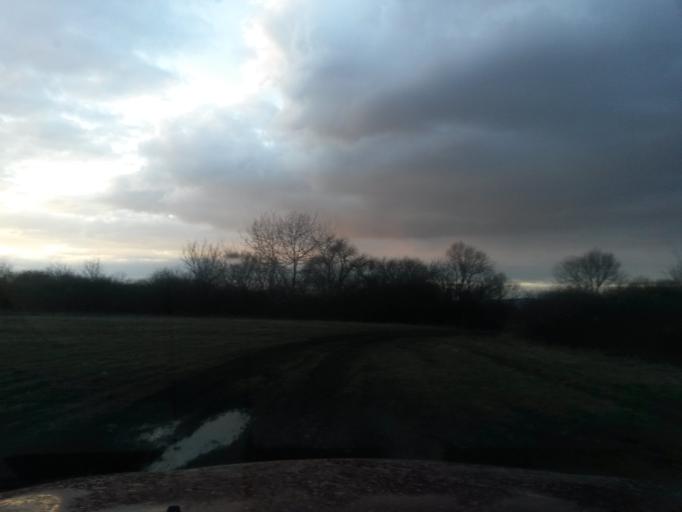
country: SK
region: Kosicky
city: Sobrance
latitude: 48.7025
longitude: 22.0711
